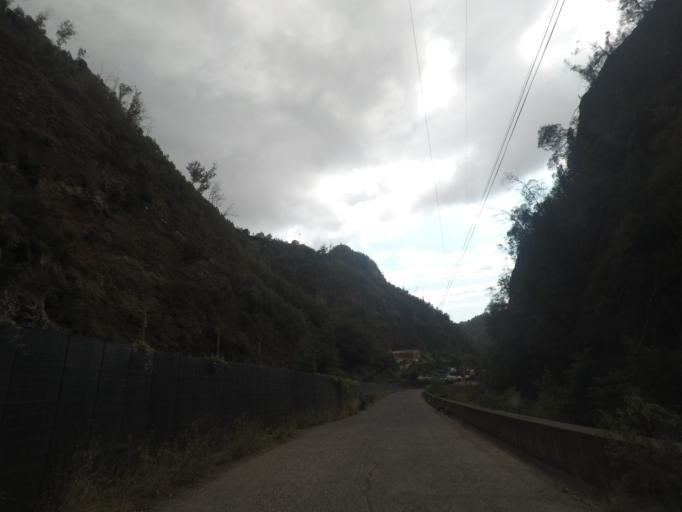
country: PT
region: Madeira
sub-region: Funchal
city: Nossa Senhora do Monte
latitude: 32.6834
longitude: -16.9150
